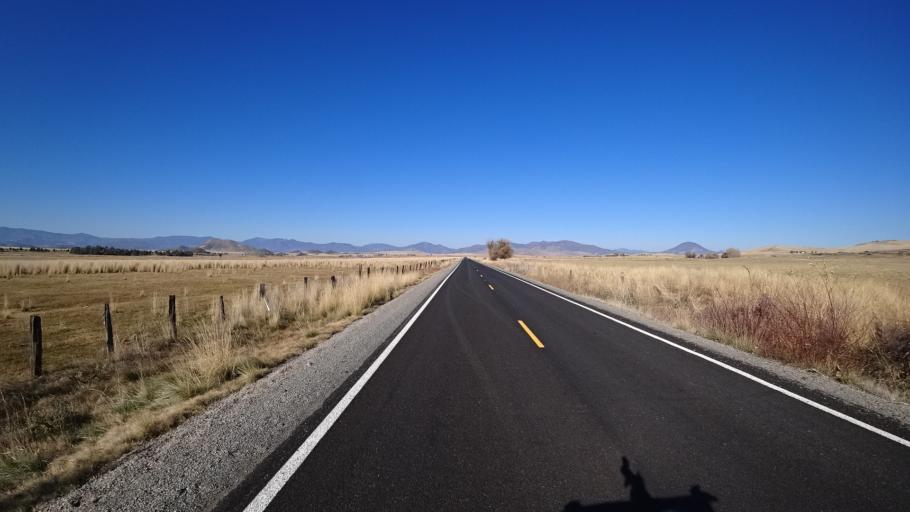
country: US
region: California
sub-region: Siskiyou County
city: Montague
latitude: 41.7152
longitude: -122.4435
